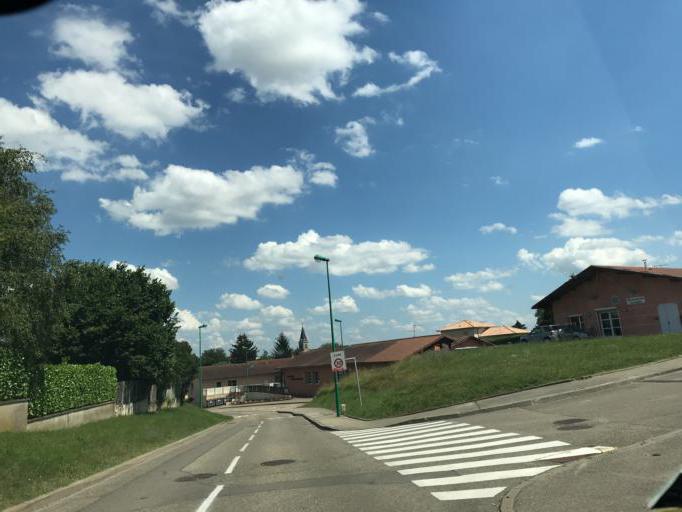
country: FR
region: Rhone-Alpes
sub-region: Departement de l'Ain
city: Mionnay
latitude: 45.8955
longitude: 4.9280
